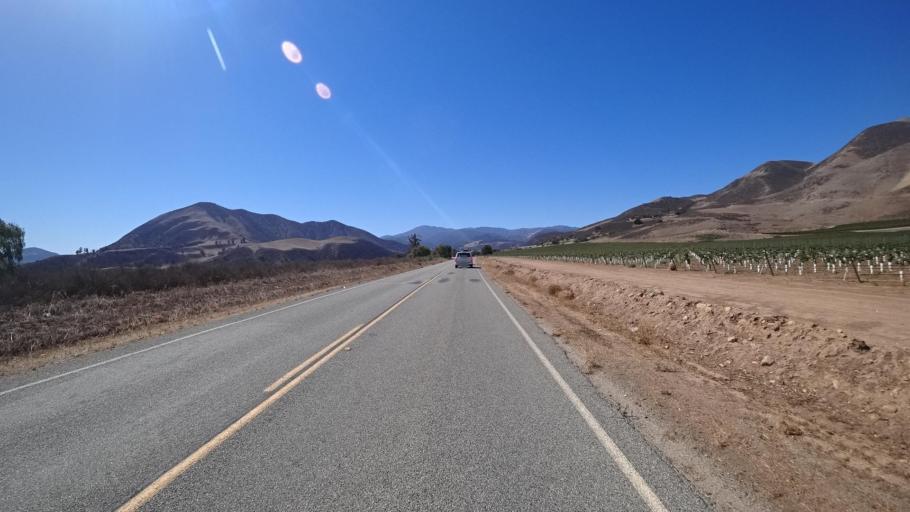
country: US
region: California
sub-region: Monterey County
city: Greenfield
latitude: 36.2893
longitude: -121.3144
